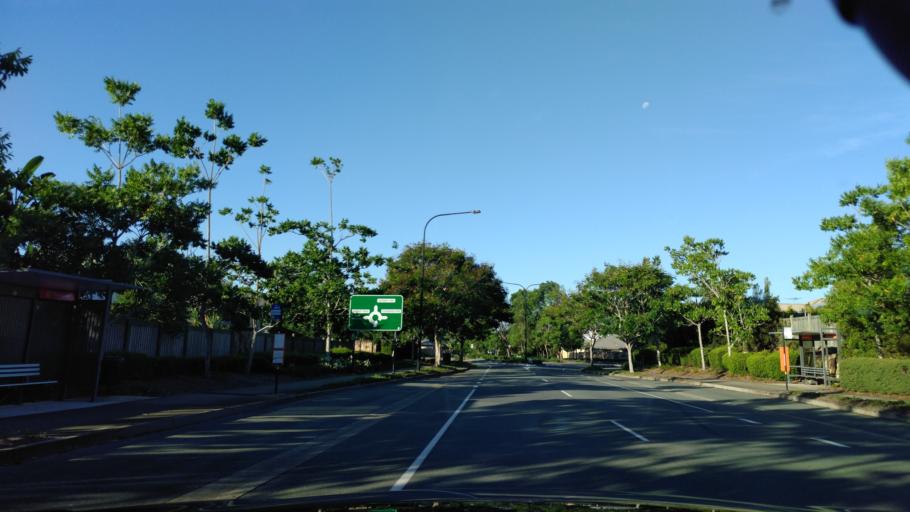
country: AU
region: Queensland
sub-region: Moreton Bay
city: Deception Bay
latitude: -27.2132
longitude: 153.0238
